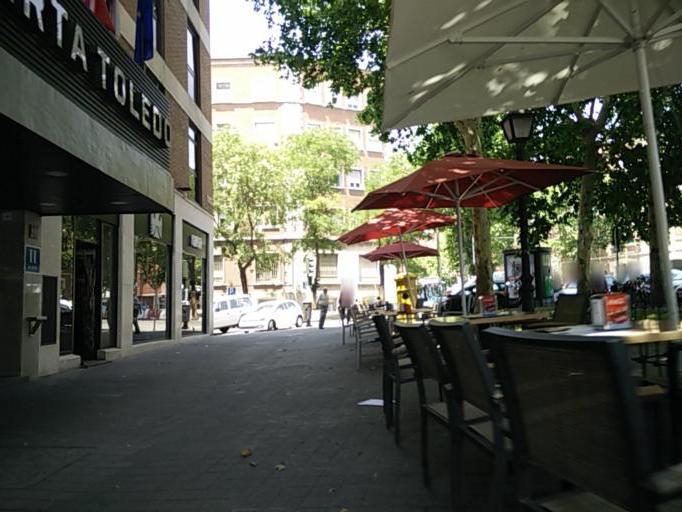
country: ES
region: Madrid
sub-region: Provincia de Madrid
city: Madrid
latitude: 40.4063
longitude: -3.7121
